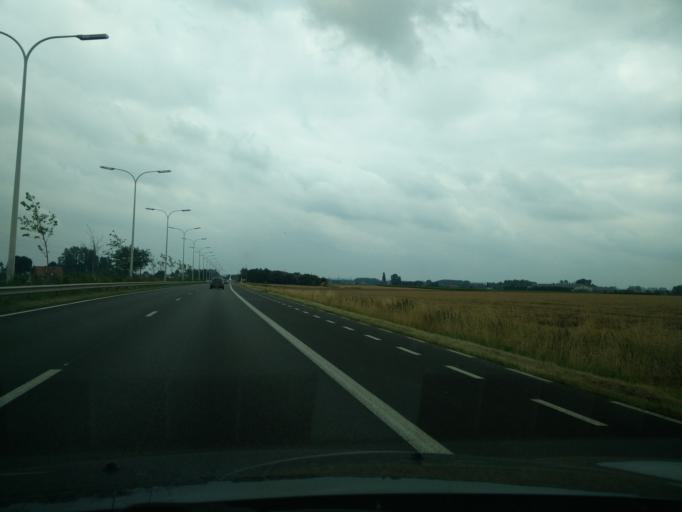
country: BE
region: Flanders
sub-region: Provincie Oost-Vlaanderen
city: Oudenaarde
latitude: 50.8881
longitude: 3.6159
